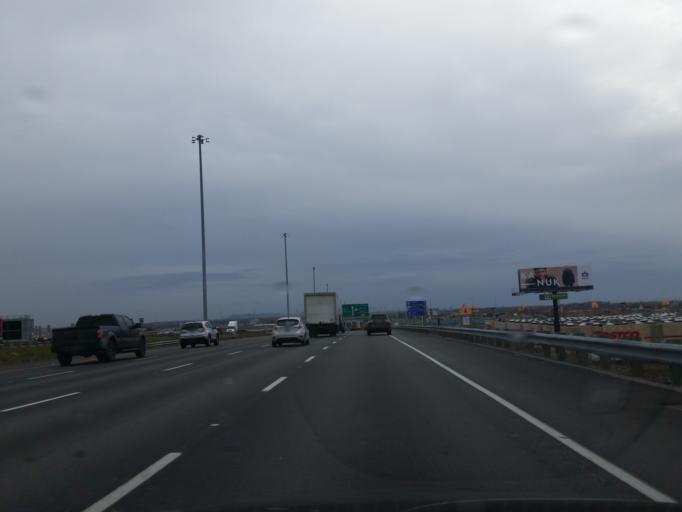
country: CA
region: Quebec
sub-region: Laurentides
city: Sainte-Therese
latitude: 45.6346
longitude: -73.8514
